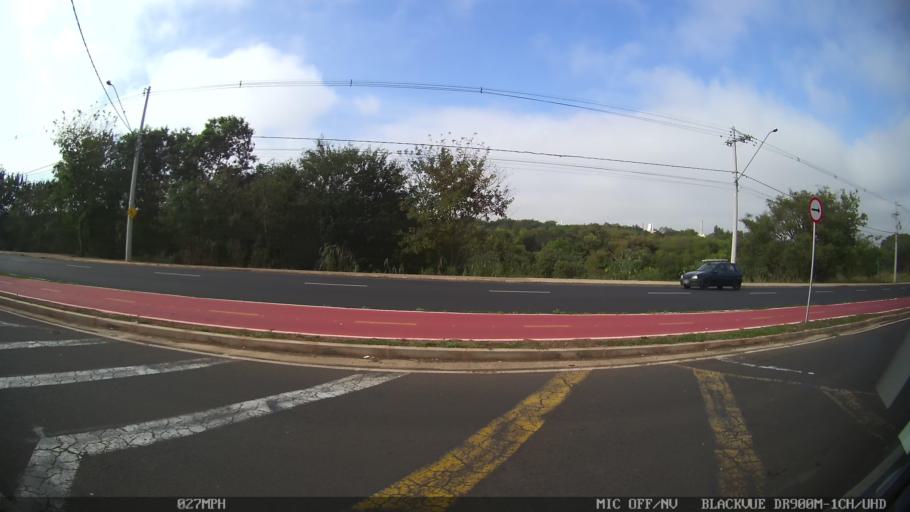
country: BR
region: Sao Paulo
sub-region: Sao Jose Do Rio Preto
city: Sao Jose do Rio Preto
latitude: -20.8088
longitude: -49.4303
